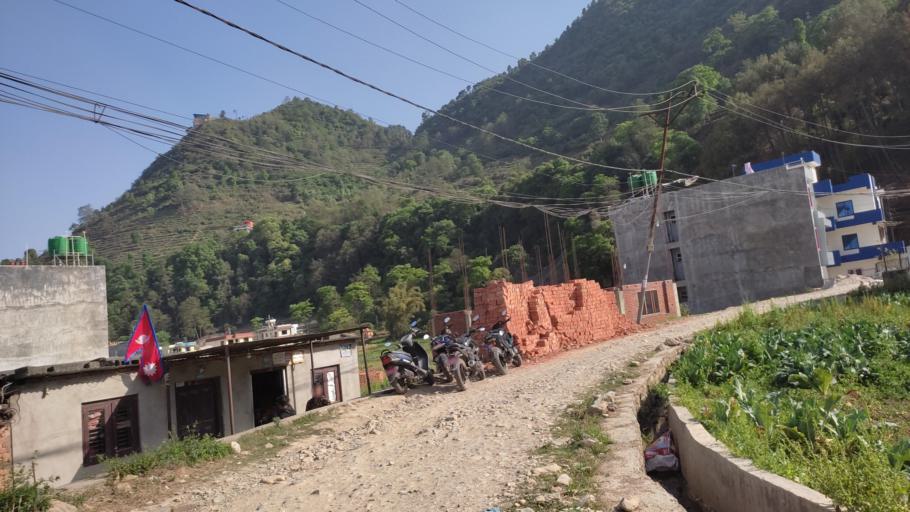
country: NP
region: Central Region
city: Kirtipur
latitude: 27.6592
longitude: 85.2650
